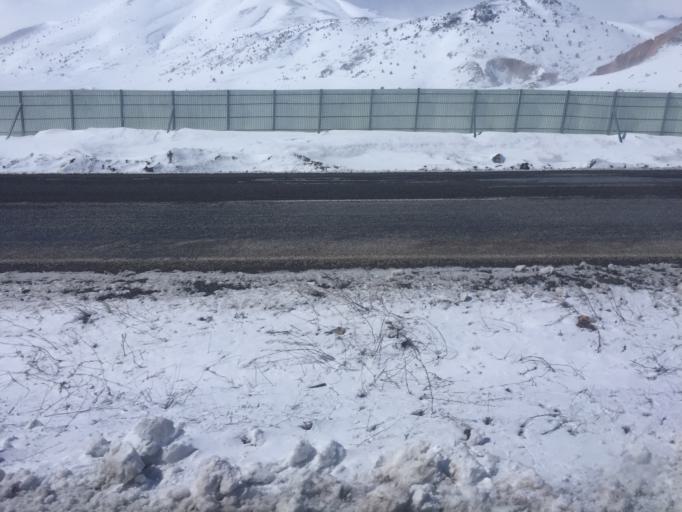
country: TR
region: Kahramanmaras
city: Goksun
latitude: 38.1821
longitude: 36.4568
